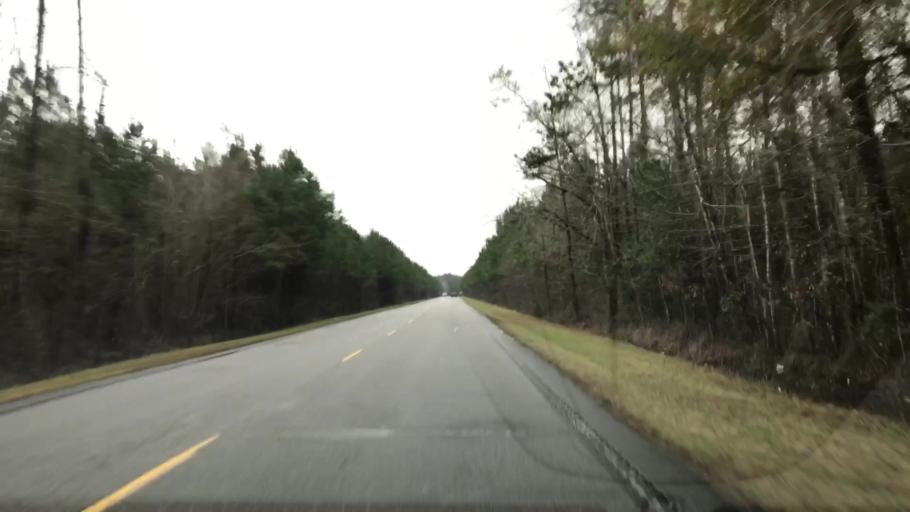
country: US
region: South Carolina
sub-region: Williamsburg County
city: Andrews
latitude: 33.5694
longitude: -79.4518
